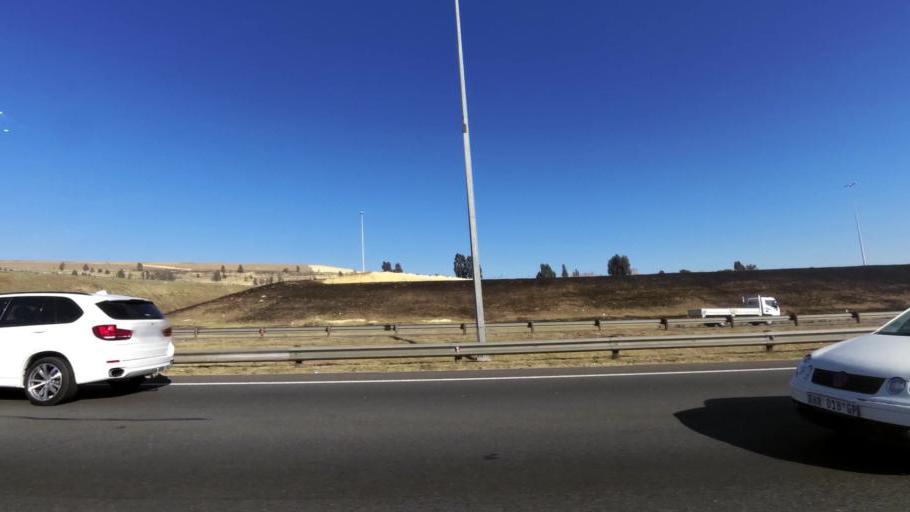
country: ZA
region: Gauteng
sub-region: City of Johannesburg Metropolitan Municipality
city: Johannesburg
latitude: -26.2170
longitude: 27.9596
